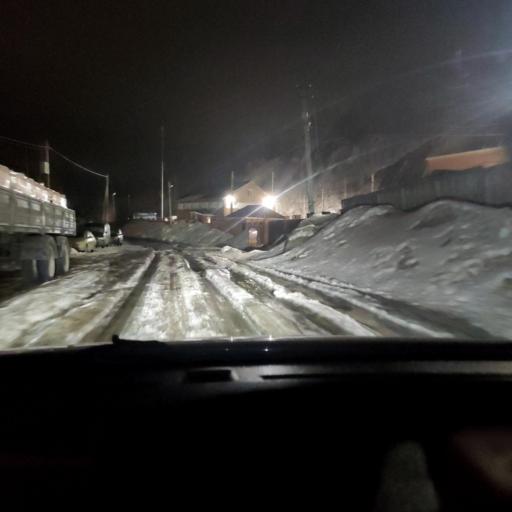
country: RU
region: Tatarstan
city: Vysokaya Gora
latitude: 55.8642
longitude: 49.2456
